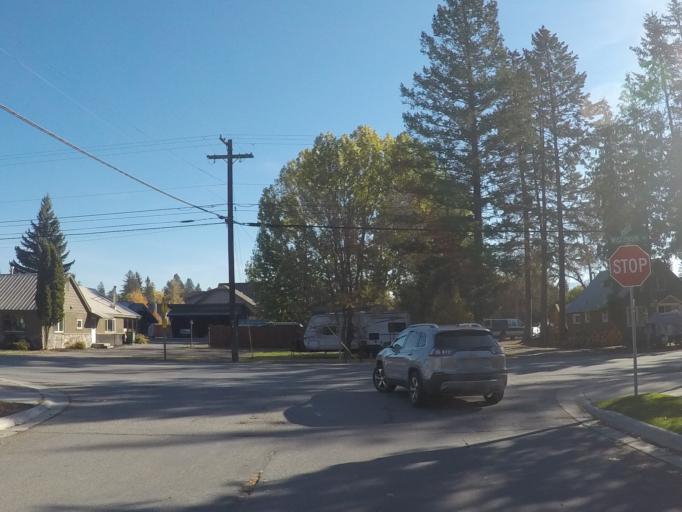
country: US
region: Montana
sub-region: Flathead County
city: Whitefish
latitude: 48.4180
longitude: -114.3414
